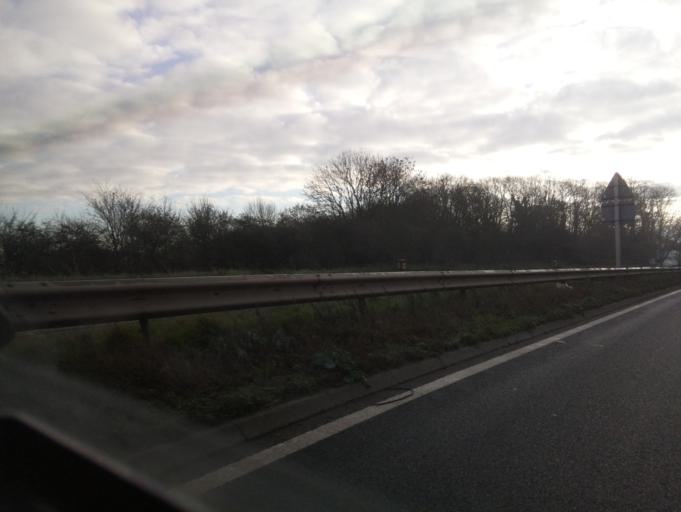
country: GB
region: England
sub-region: Staffordshire
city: Lichfield
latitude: 52.6598
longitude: -1.8112
